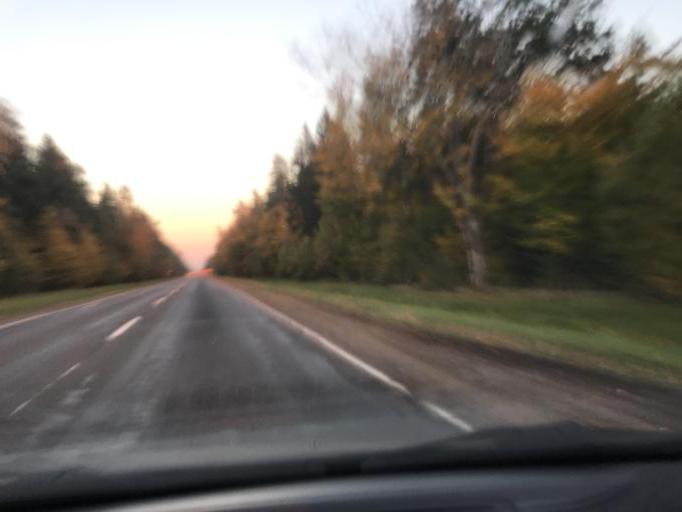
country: BY
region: Mogilev
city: Hlusha
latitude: 53.1014
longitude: 29.0293
